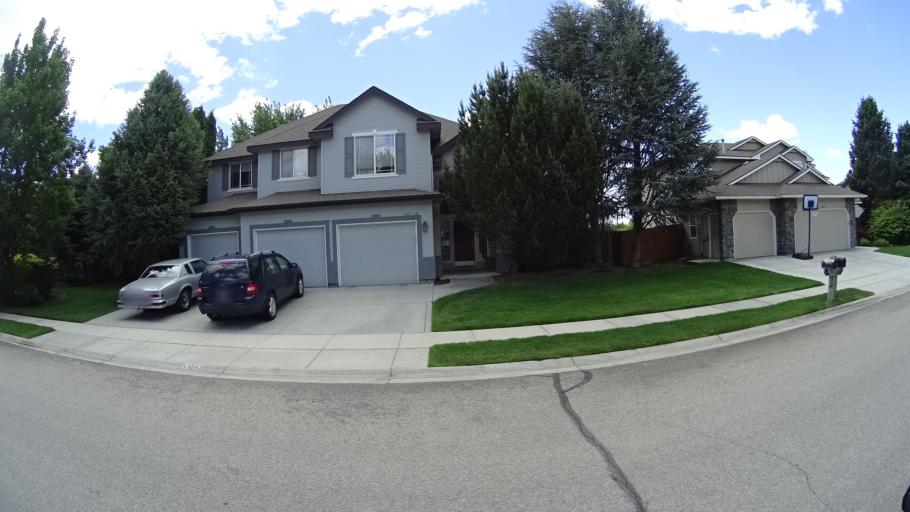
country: US
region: Idaho
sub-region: Ada County
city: Eagle
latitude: 43.6525
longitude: -116.3517
